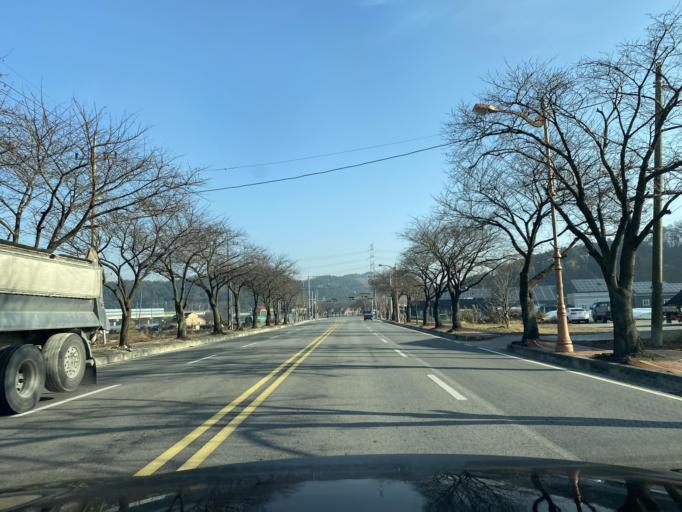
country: KR
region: Chungcheongnam-do
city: Yesan
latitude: 36.7321
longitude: 126.8596
